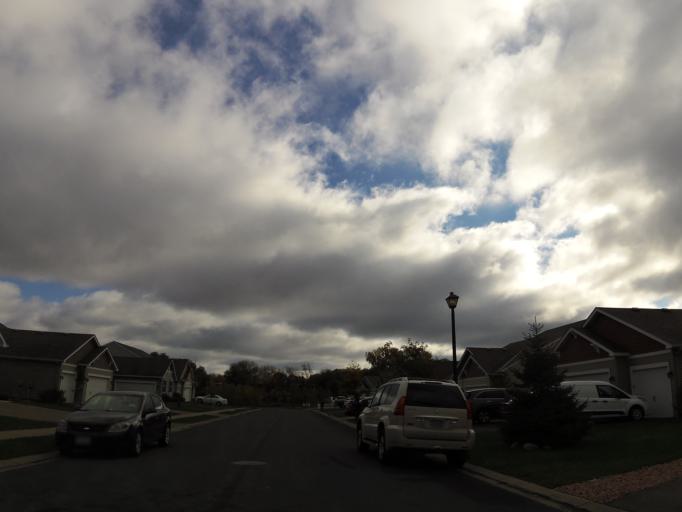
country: US
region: Minnesota
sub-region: Scott County
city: Savage
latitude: 44.7747
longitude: -93.3311
